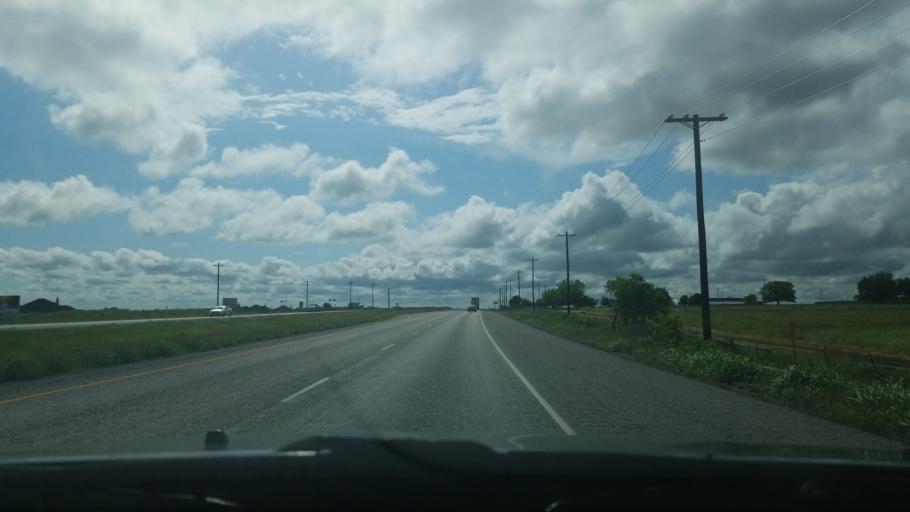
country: US
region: Texas
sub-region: Denton County
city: Ponder
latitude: 33.2418
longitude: -97.3629
